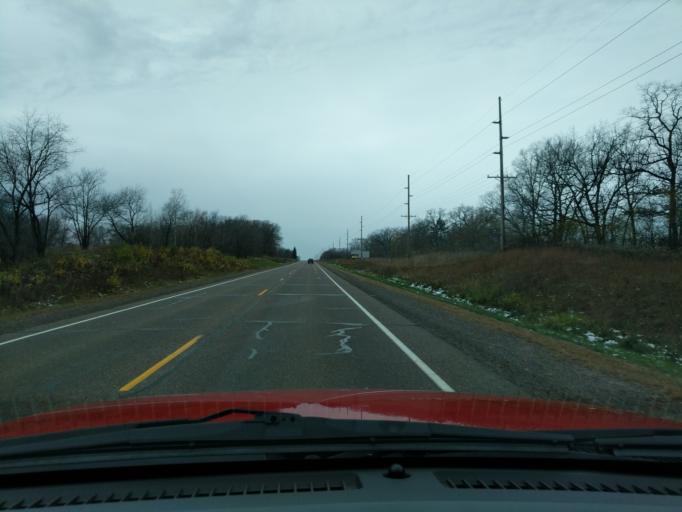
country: US
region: Wisconsin
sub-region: Washburn County
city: Shell Lake
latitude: 45.8153
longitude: -92.0225
